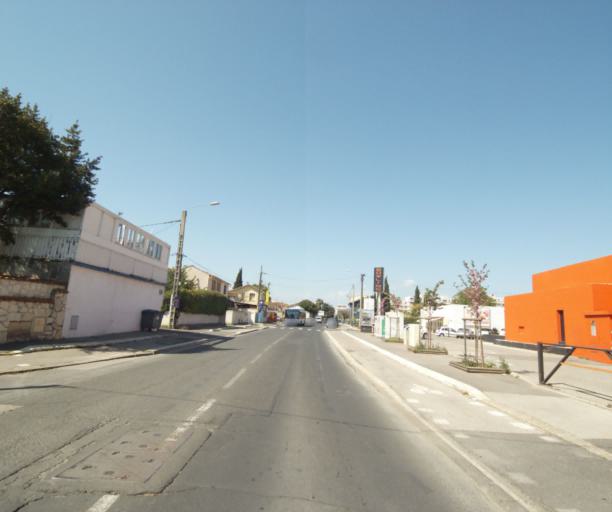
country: FR
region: Languedoc-Roussillon
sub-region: Departement de l'Herault
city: Montpellier
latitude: 43.6116
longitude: 3.8984
